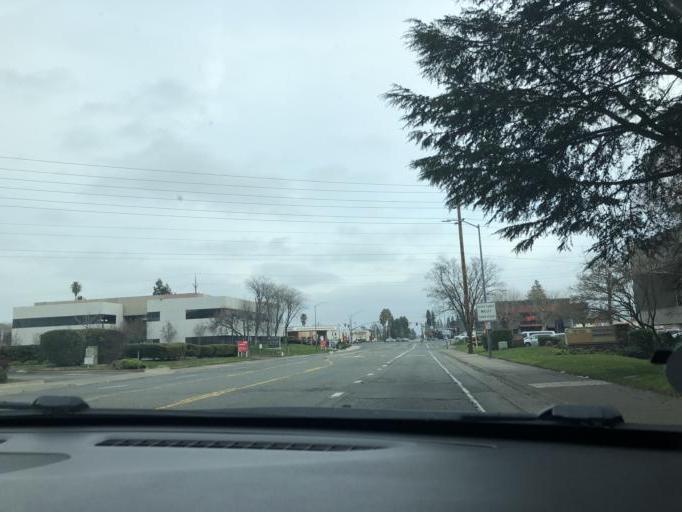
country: US
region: California
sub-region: Sacramento County
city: Arden-Arcade
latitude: 38.5889
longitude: -121.4176
